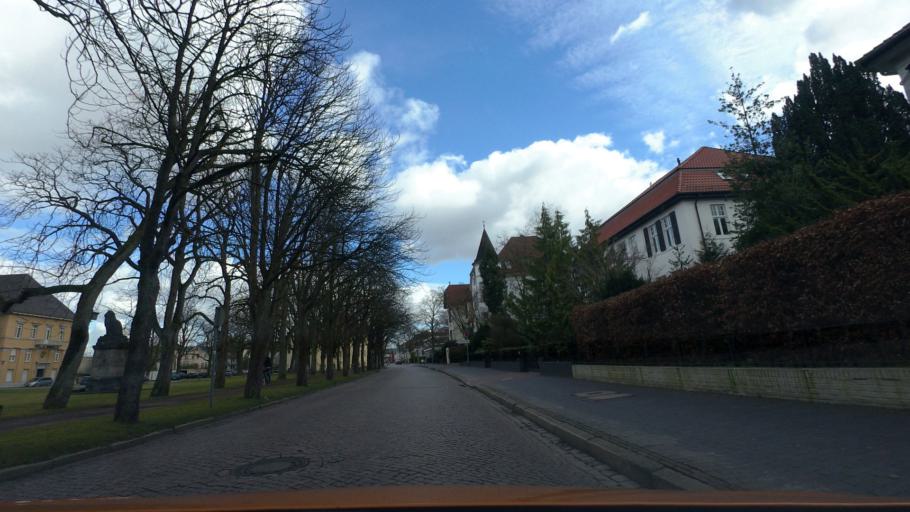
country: DE
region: Lower Saxony
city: Oldenburg
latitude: 53.1380
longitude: 8.2020
